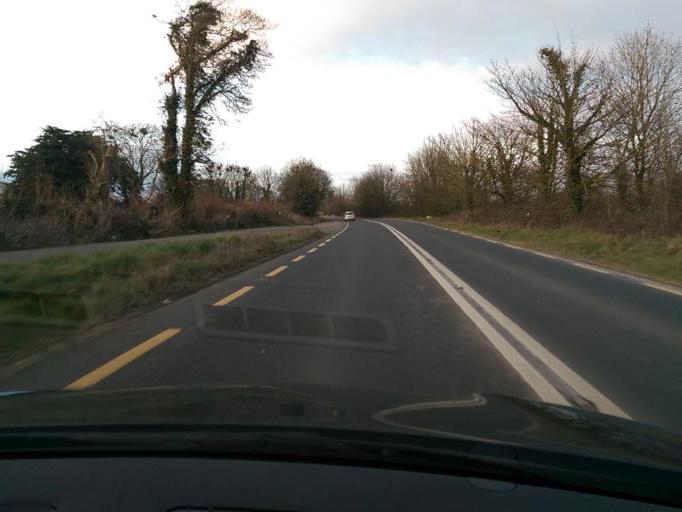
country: IE
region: Munster
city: Nenagh Bridge
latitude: 52.9005
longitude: -8.1862
